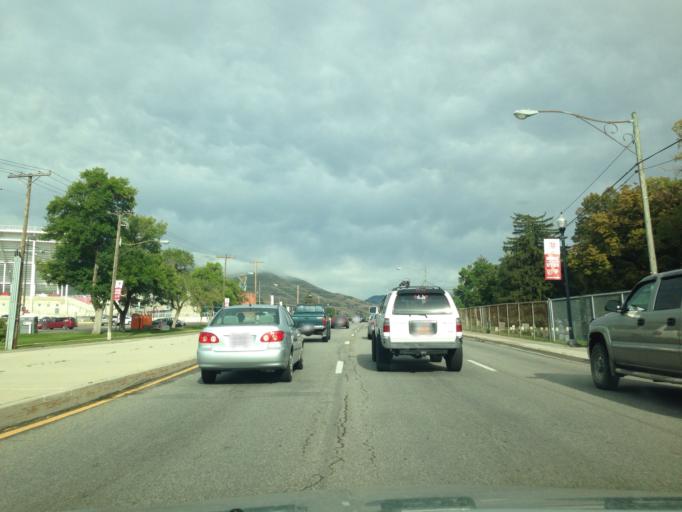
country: US
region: Utah
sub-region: Salt Lake County
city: Salt Lake City
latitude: 40.7584
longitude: -111.8518
